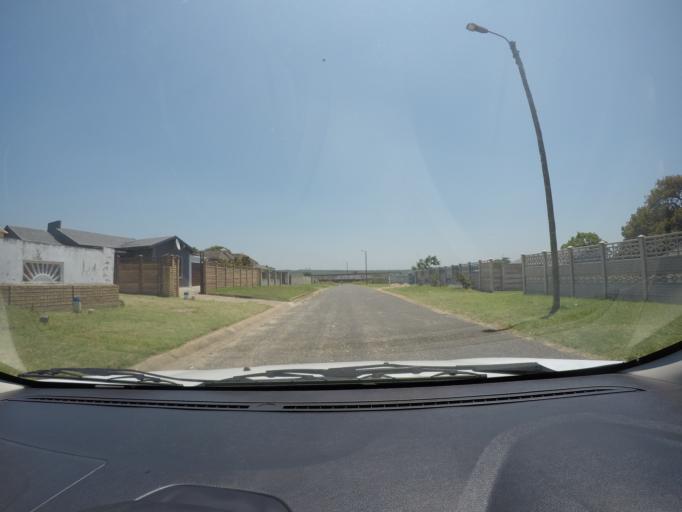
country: ZA
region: KwaZulu-Natal
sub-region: uThungulu District Municipality
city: eSikhawini
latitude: -28.8768
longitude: 31.9060
